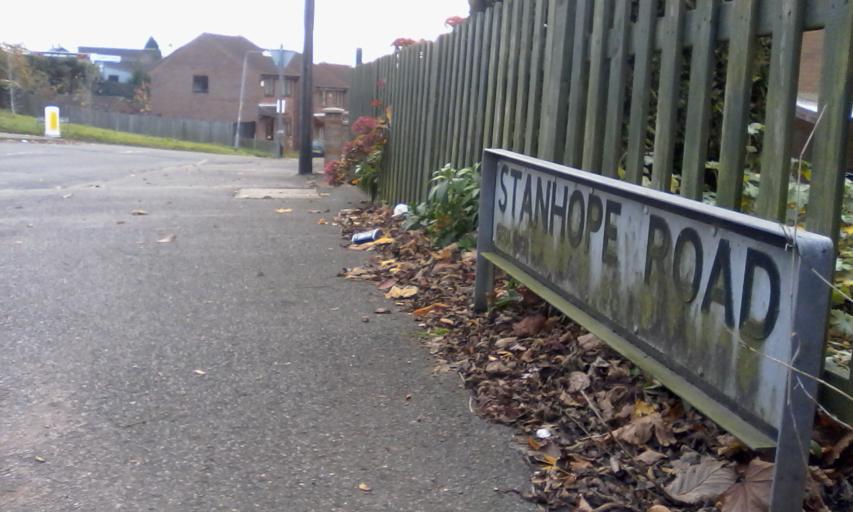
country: GB
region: England
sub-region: Nottinghamshire
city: Arnold
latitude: 52.9864
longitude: -1.0966
